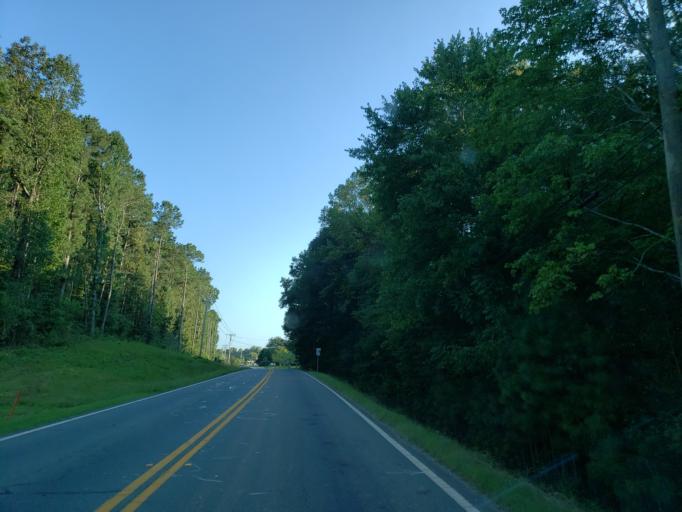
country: US
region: Georgia
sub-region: Murray County
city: Chatsworth
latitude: 34.7337
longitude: -84.8206
